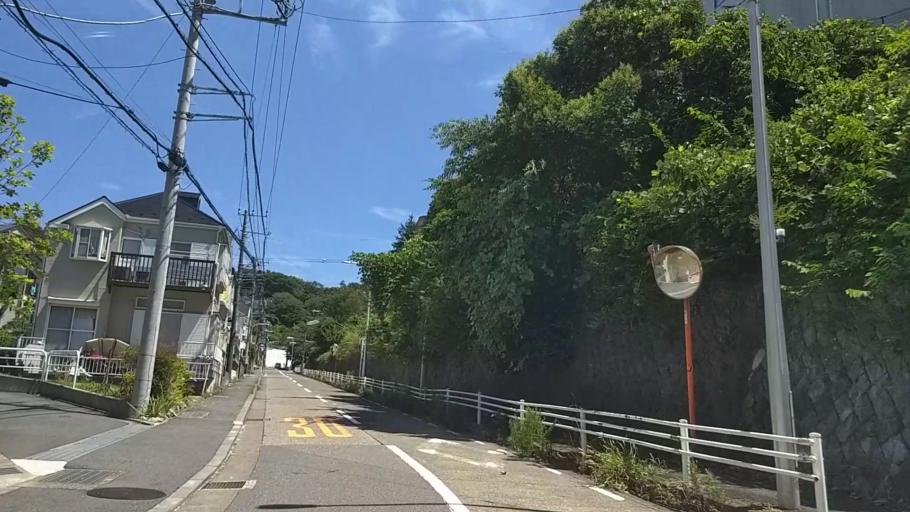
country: JP
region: Kanagawa
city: Zushi
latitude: 35.3049
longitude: 139.5970
